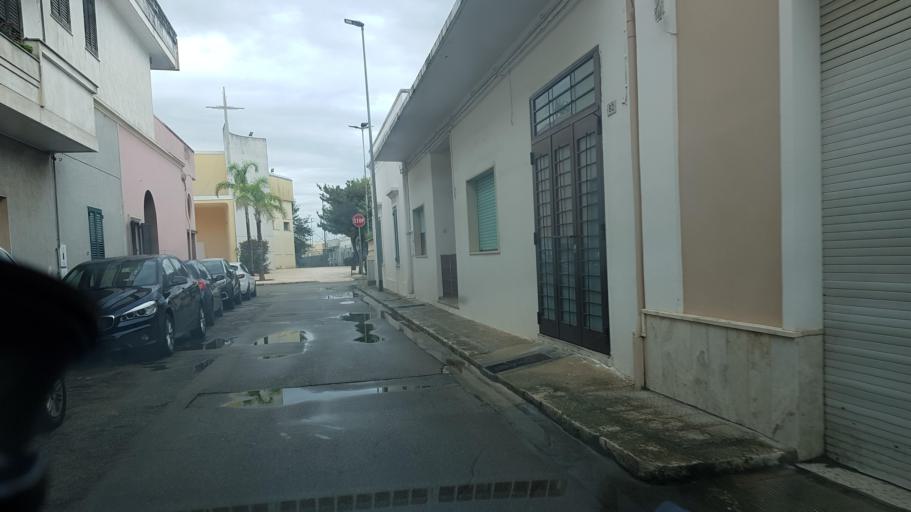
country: IT
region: Apulia
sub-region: Provincia di Lecce
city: Carmiano
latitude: 40.3478
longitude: 18.0395
